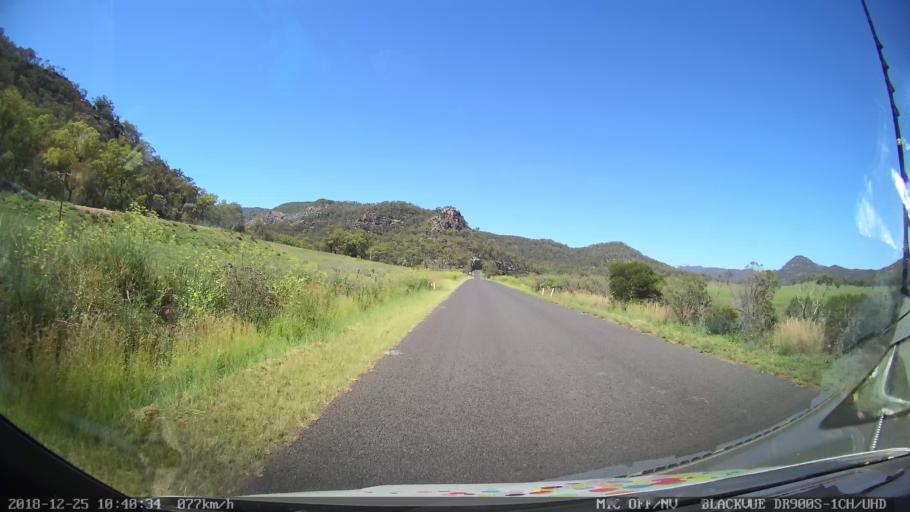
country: AU
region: New South Wales
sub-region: Upper Hunter Shire
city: Merriwa
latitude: -32.4090
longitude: 150.3422
